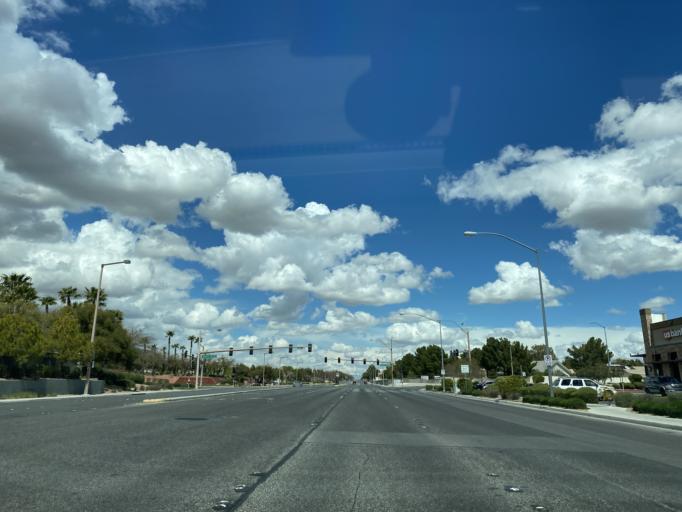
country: US
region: Nevada
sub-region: Clark County
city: Summerlin South
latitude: 36.1287
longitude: -115.3151
